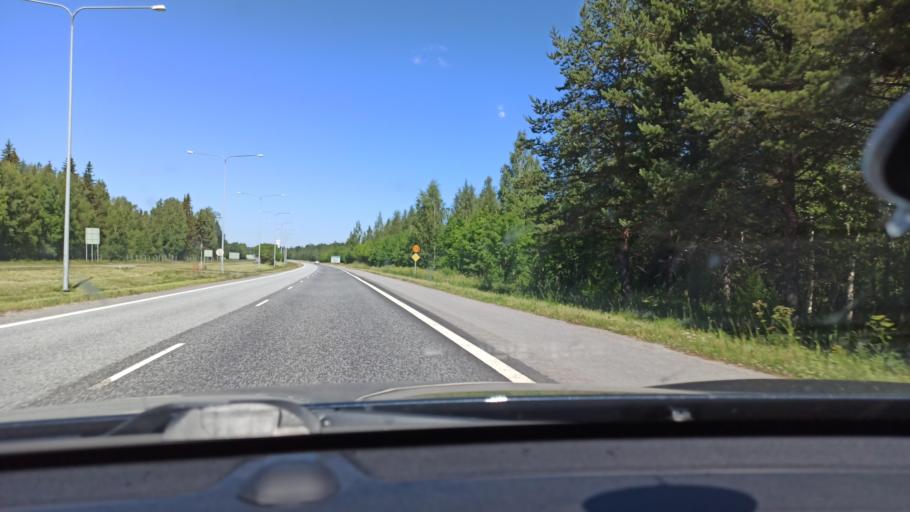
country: FI
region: Ostrobothnia
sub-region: Vaasa
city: Ristinummi
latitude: 63.0606
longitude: 21.7095
